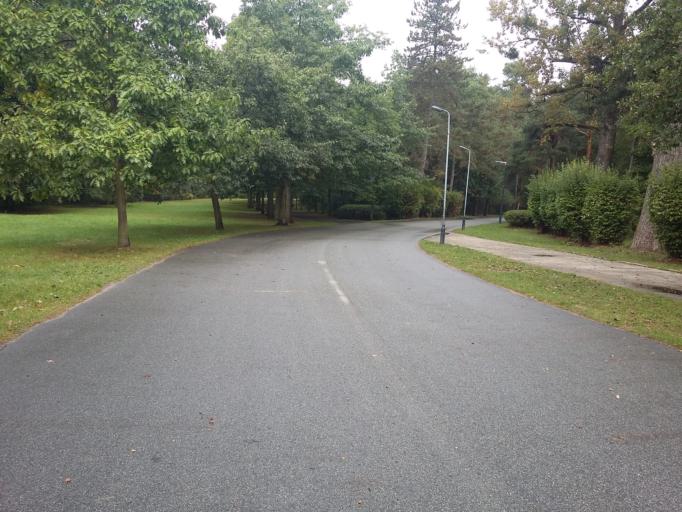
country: PL
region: Lodz Voivodeship
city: Lodz
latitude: 51.7665
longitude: 19.4102
